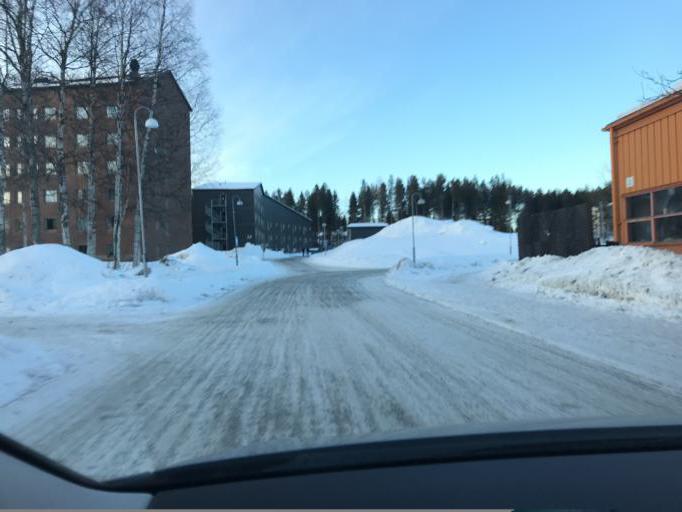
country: SE
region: Norrbotten
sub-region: Lulea Kommun
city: Lulea
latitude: 65.6197
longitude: 22.1404
